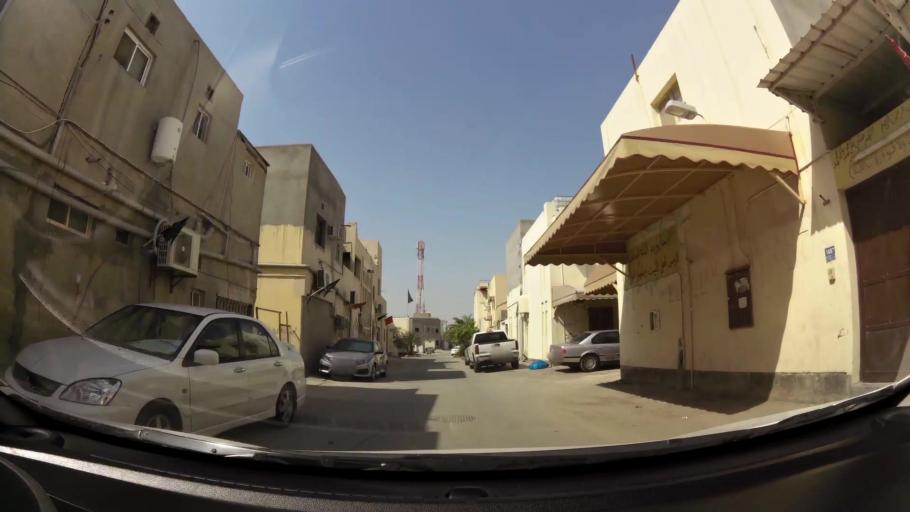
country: BH
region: Northern
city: Madinat `Isa
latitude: 26.1958
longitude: 50.4649
